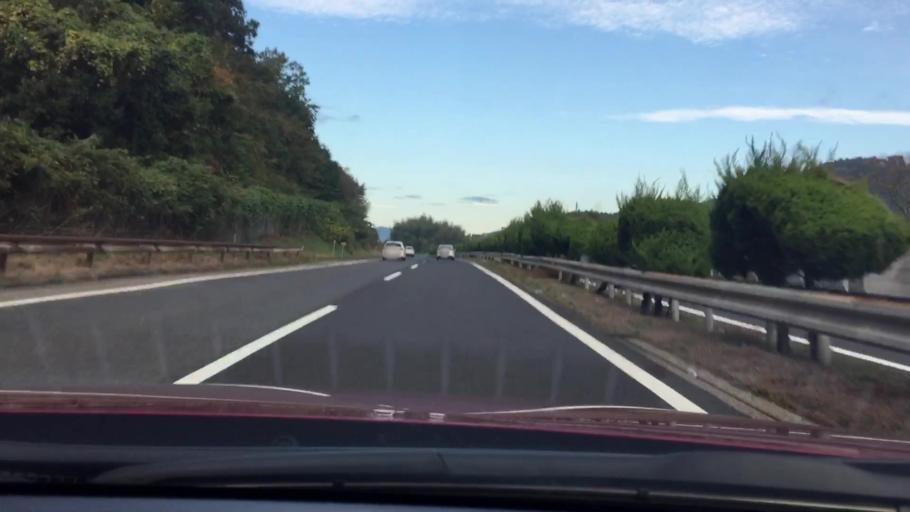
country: JP
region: Hyogo
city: Himeji
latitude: 34.9587
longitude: 134.7070
